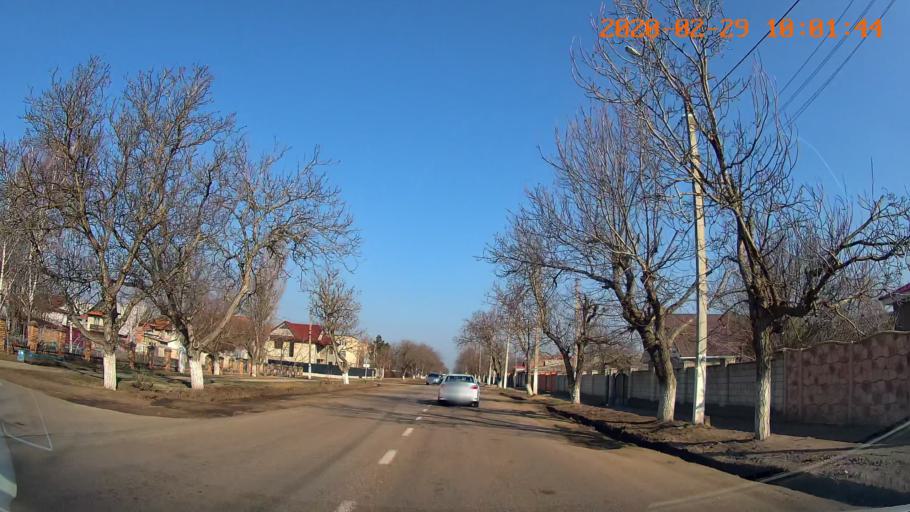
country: MD
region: Telenesti
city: Slobozia
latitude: 46.7774
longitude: 29.6844
